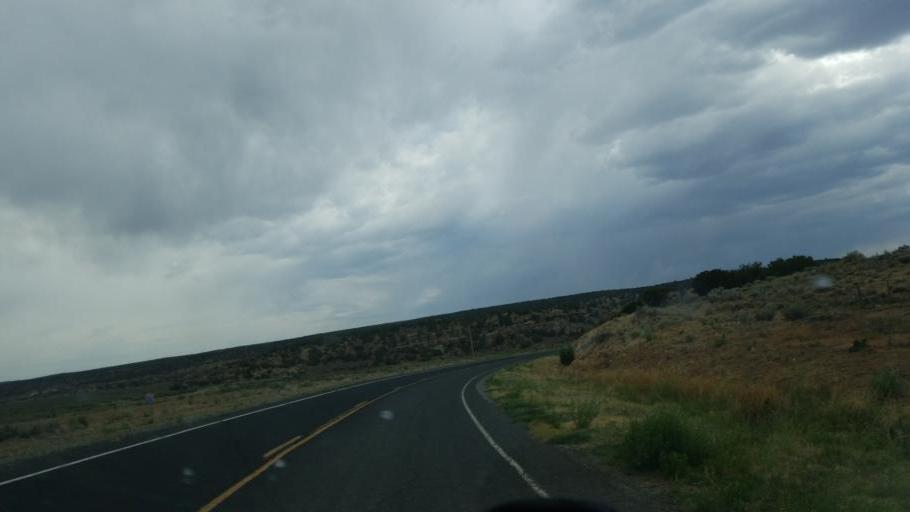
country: US
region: Arizona
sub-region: Apache County
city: Saint Michaels
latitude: 35.4173
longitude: -108.9814
